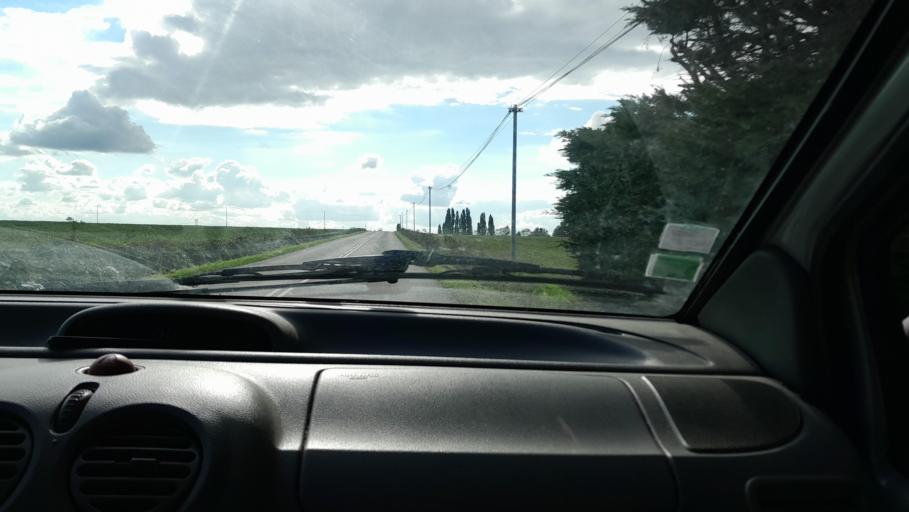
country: FR
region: Brittany
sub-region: Departement d'Ille-et-Vilaine
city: Le Pertre
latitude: 47.9922
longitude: -0.9884
